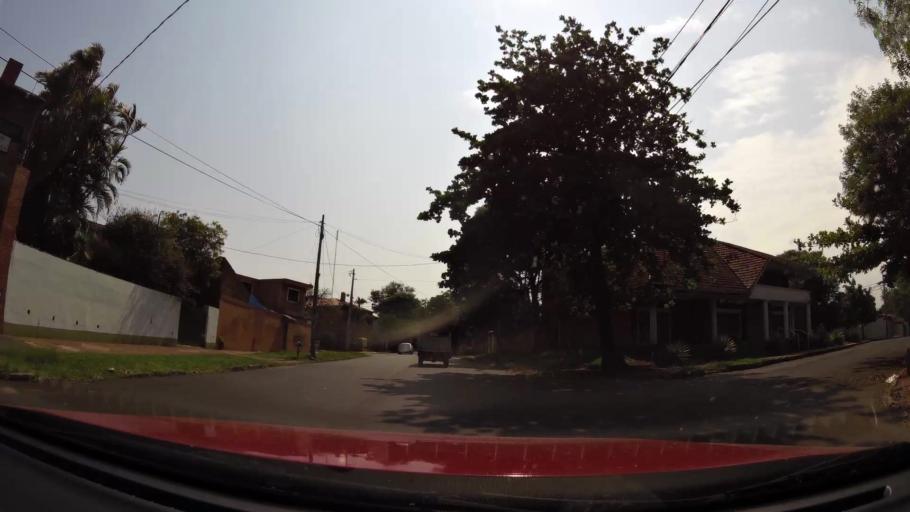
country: PY
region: Asuncion
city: Asuncion
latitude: -25.2925
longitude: -57.6546
